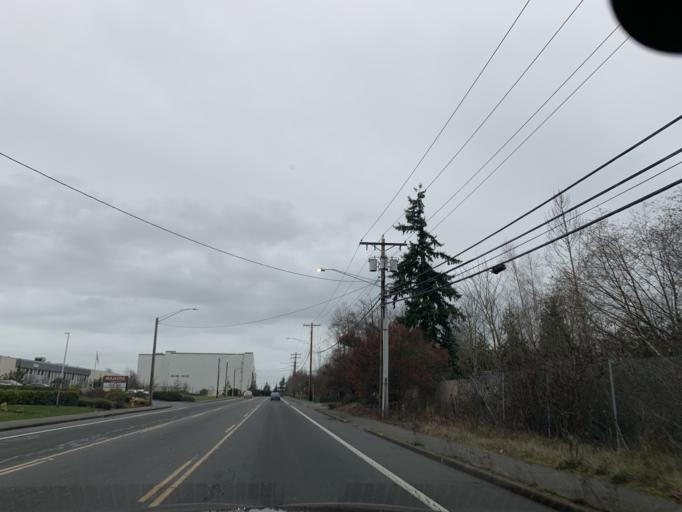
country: US
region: Washington
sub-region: Snohomish County
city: Mukilteo
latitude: 47.9201
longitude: -122.2667
